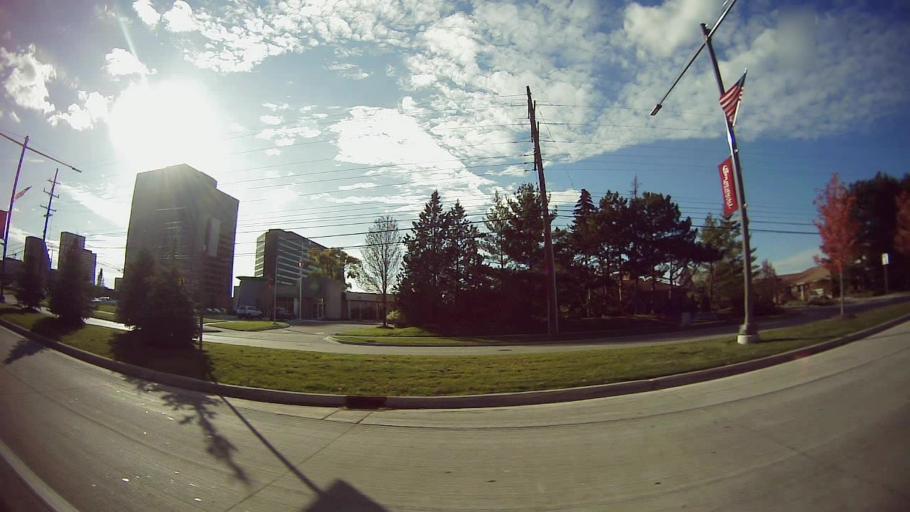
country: US
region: Michigan
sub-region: Oakland County
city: Lathrup Village
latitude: 42.4855
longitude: -83.2410
